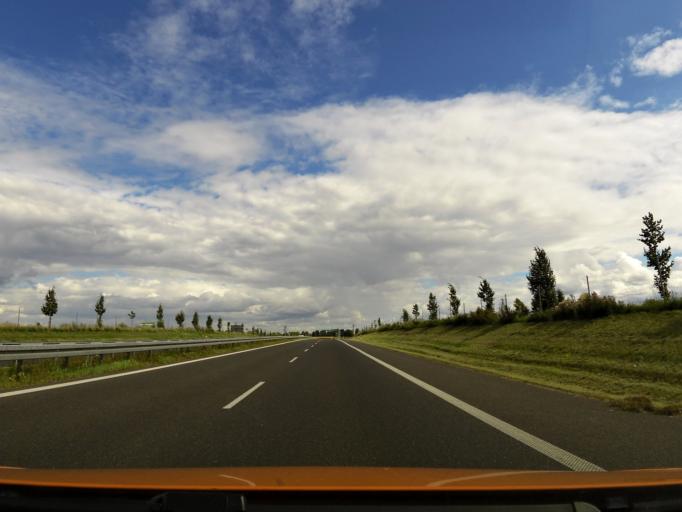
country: PL
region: West Pomeranian Voivodeship
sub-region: Powiat goleniowski
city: Nowogard
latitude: 53.6924
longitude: 15.1275
